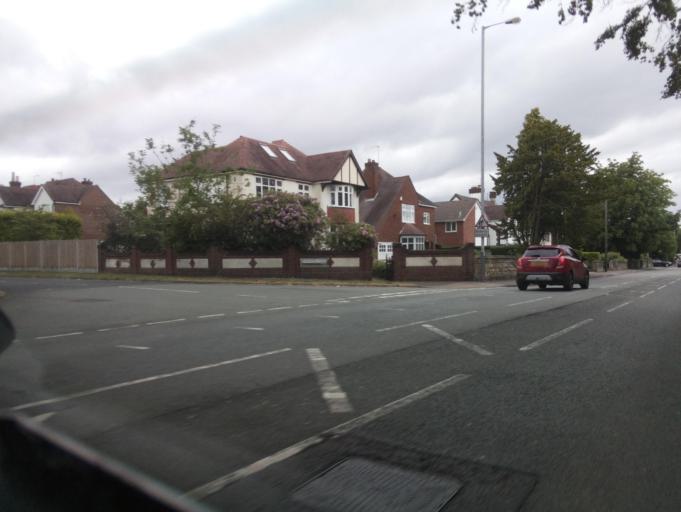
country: GB
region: England
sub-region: Wolverhampton
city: Wolverhampton
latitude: 52.5628
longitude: -2.1502
